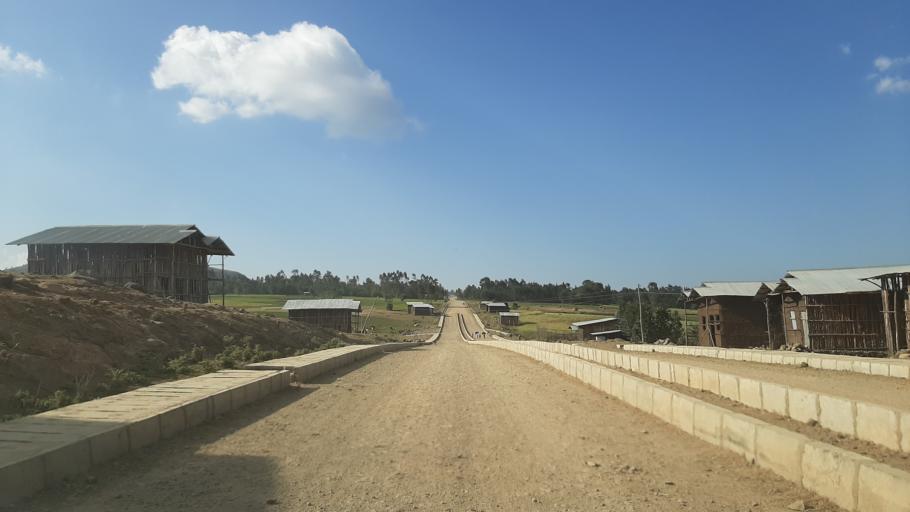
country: ET
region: Amhara
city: Dabat
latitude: 12.9934
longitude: 37.7649
